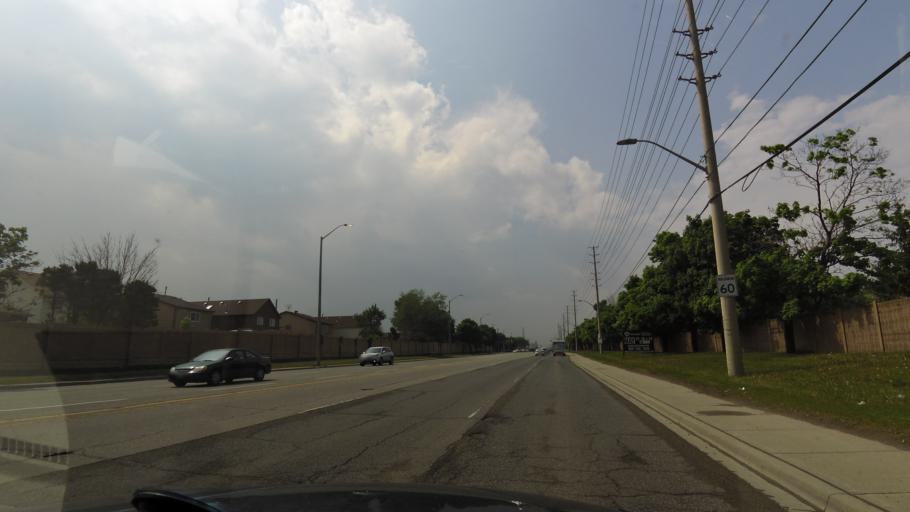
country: CA
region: Ontario
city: Mississauga
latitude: 43.5810
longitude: -79.6535
